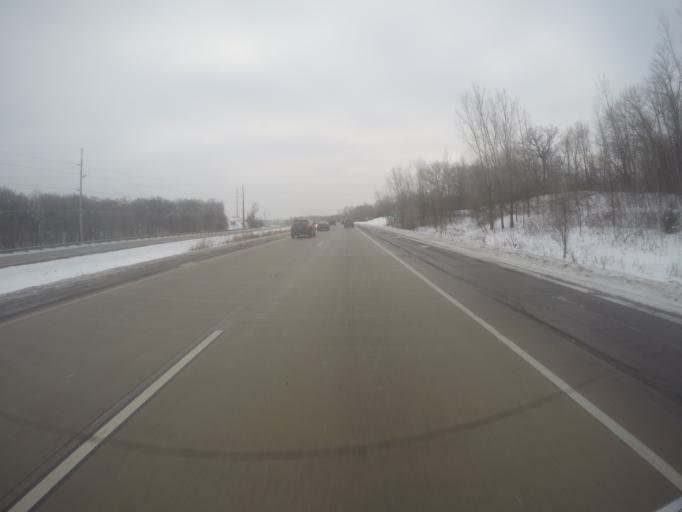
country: US
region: Minnesota
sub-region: Dakota County
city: Mendota Heights
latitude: 44.8415
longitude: -93.1035
